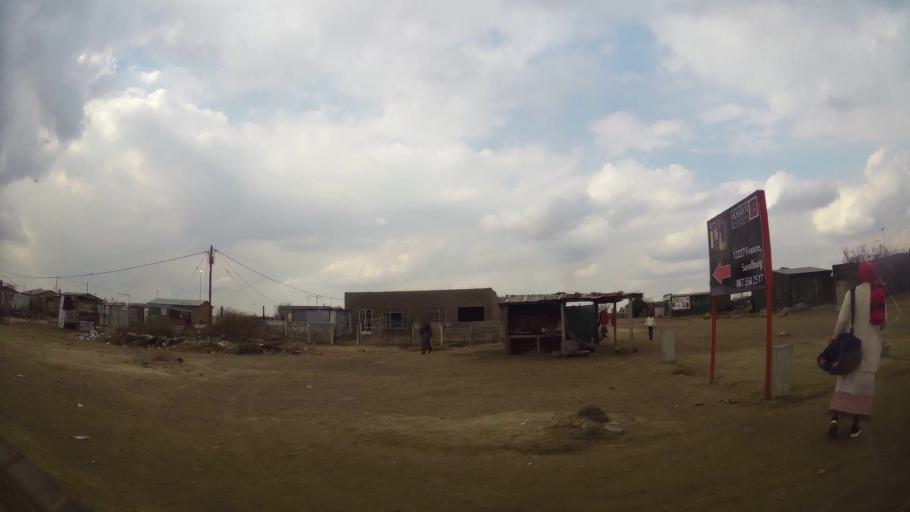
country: ZA
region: Orange Free State
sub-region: Fezile Dabi District Municipality
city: Sasolburg
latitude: -26.8624
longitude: 27.8732
